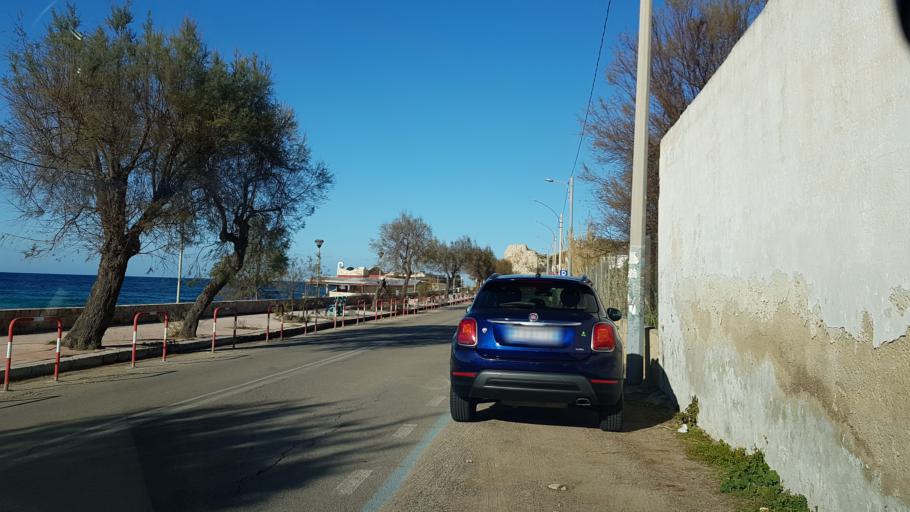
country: IT
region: Apulia
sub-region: Provincia di Lecce
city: Nardo
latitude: 40.1107
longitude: 18.0091
